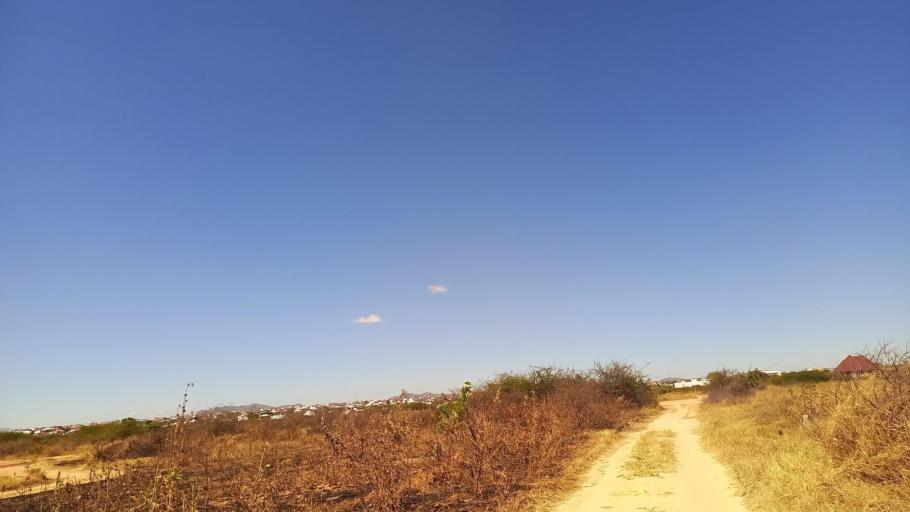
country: TZ
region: Dodoma
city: Dodoma
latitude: -6.1210
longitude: 35.6975
